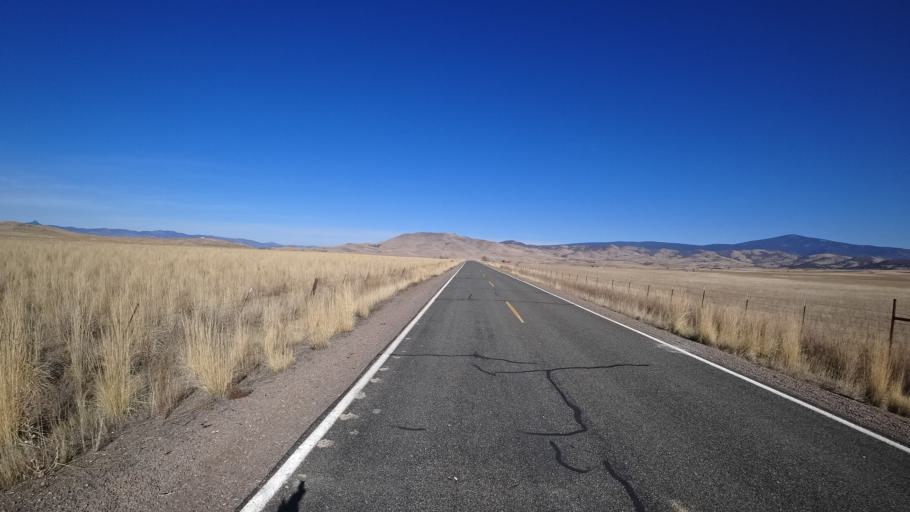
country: US
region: California
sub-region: Siskiyou County
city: Montague
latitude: 41.8026
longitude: -122.4466
